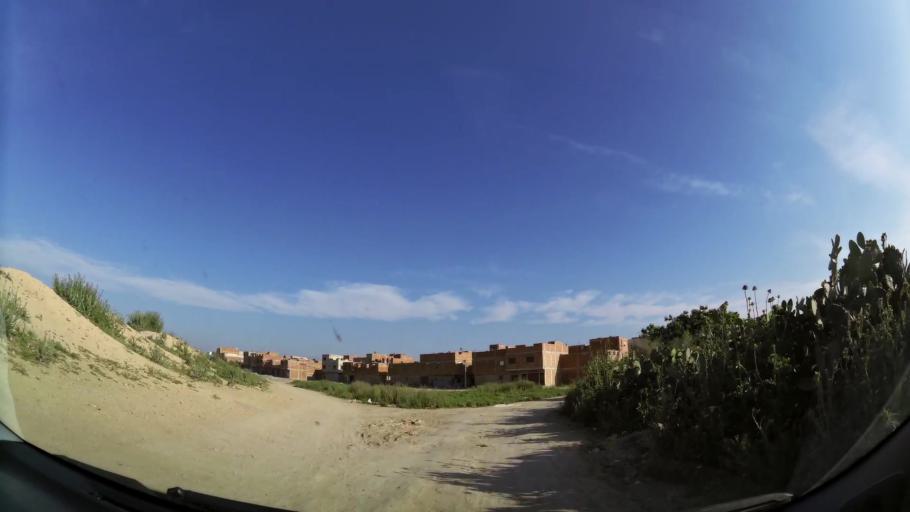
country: MA
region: Oriental
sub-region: Oujda-Angad
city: Oujda
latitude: 34.7186
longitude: -1.9052
